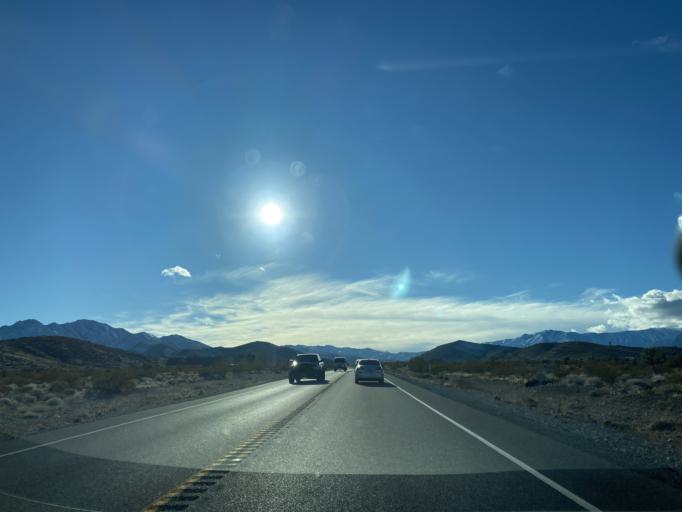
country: US
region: Nevada
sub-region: Clark County
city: Summerlin South
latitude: 36.2999
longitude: -115.4141
